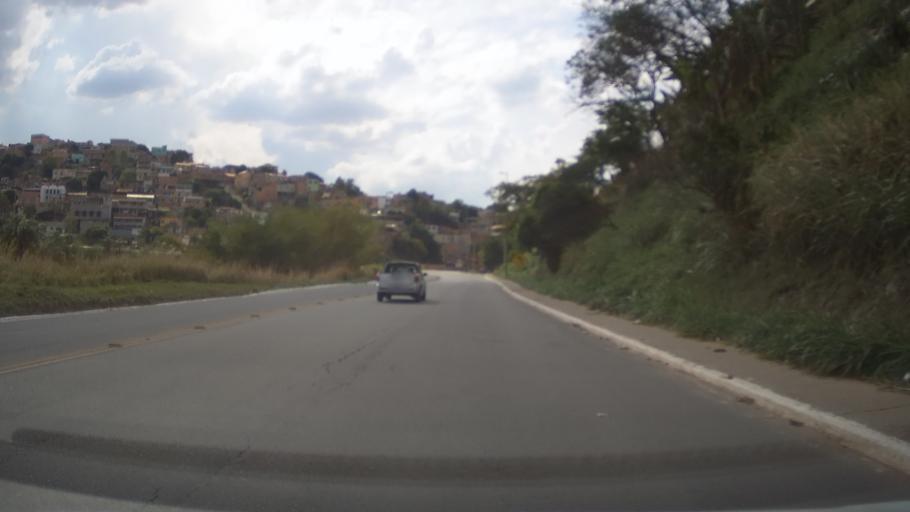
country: BR
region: Minas Gerais
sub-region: Belo Horizonte
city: Belo Horizonte
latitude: -19.8692
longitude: -43.8910
